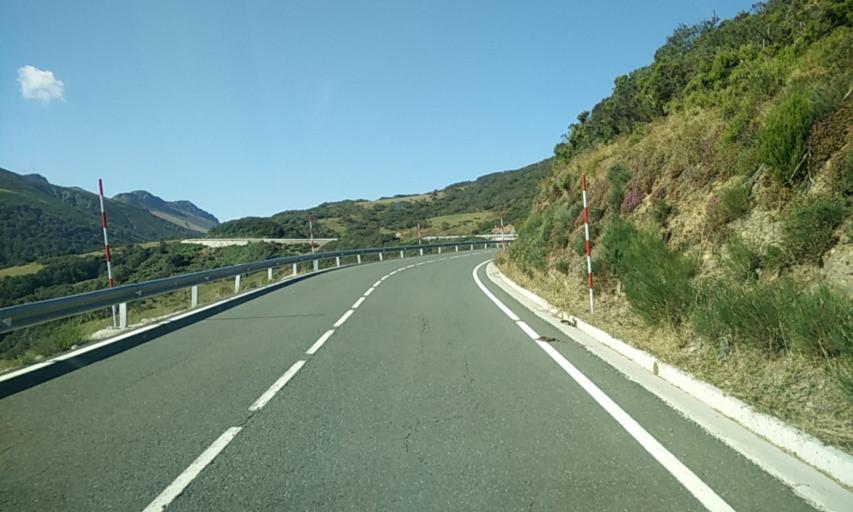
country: ES
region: Cantabria
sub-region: Provincia de Cantabria
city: Camaleno
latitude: 43.0757
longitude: -4.7362
